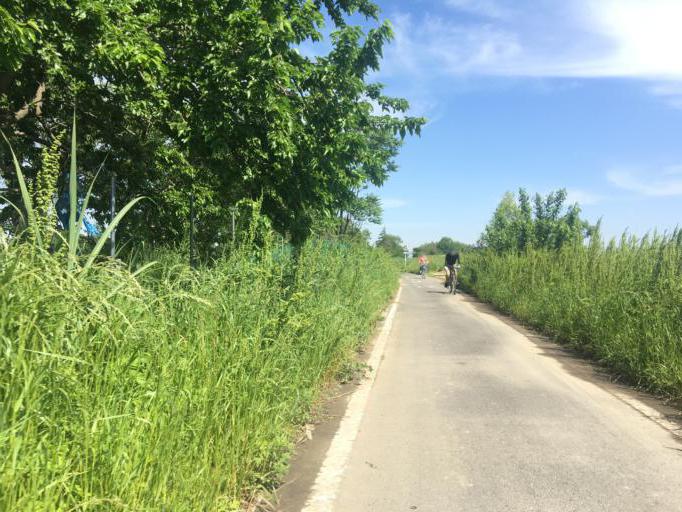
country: JP
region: Saitama
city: Shiki
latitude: 35.8691
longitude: 139.5807
